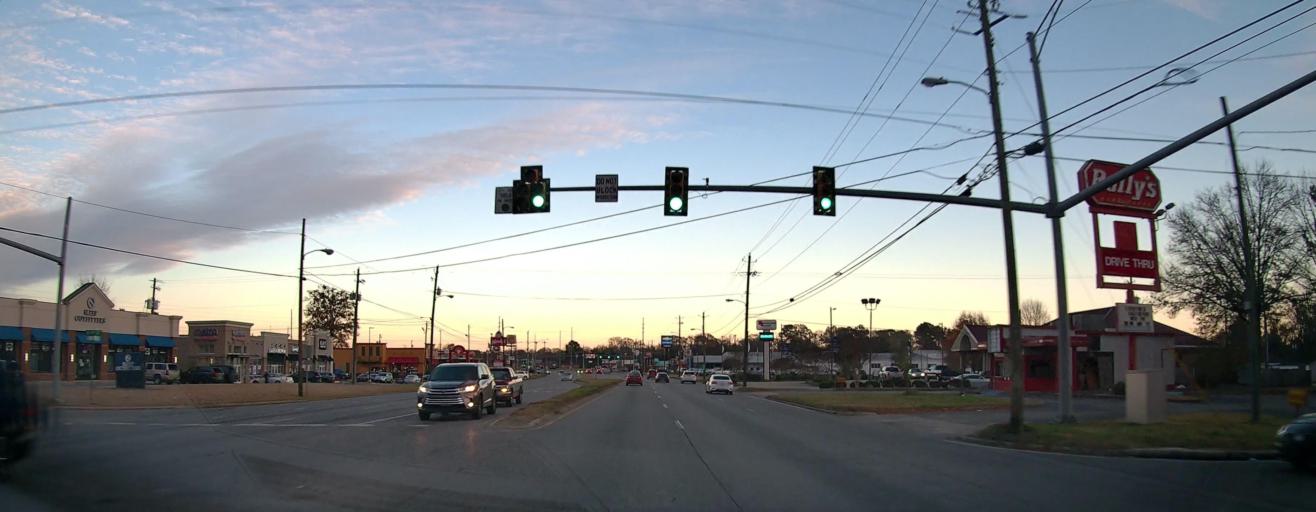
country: US
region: Alabama
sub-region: Etowah County
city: Gadsden
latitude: 34.0102
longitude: -85.9895
